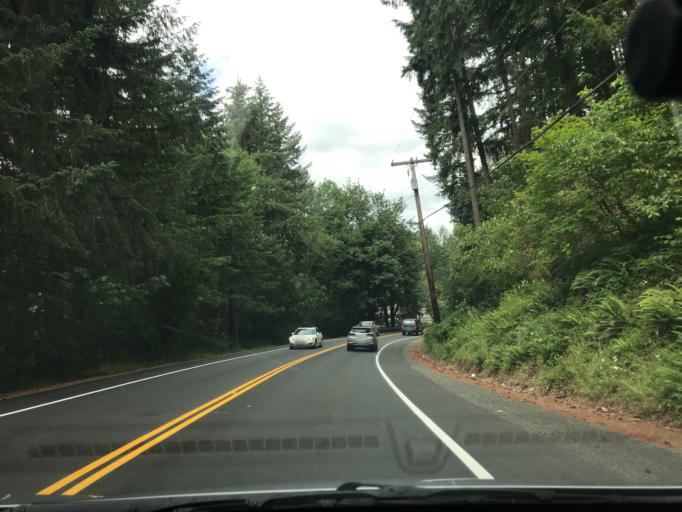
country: US
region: Washington
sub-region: King County
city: Lake Morton-Berrydale
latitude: 47.3115
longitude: -122.0978
